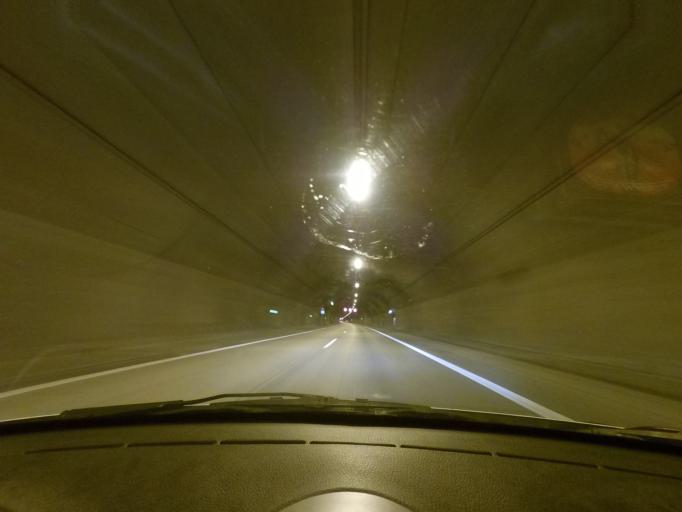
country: DE
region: Saxony
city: Bannewitz
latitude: 51.0171
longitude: 13.7010
